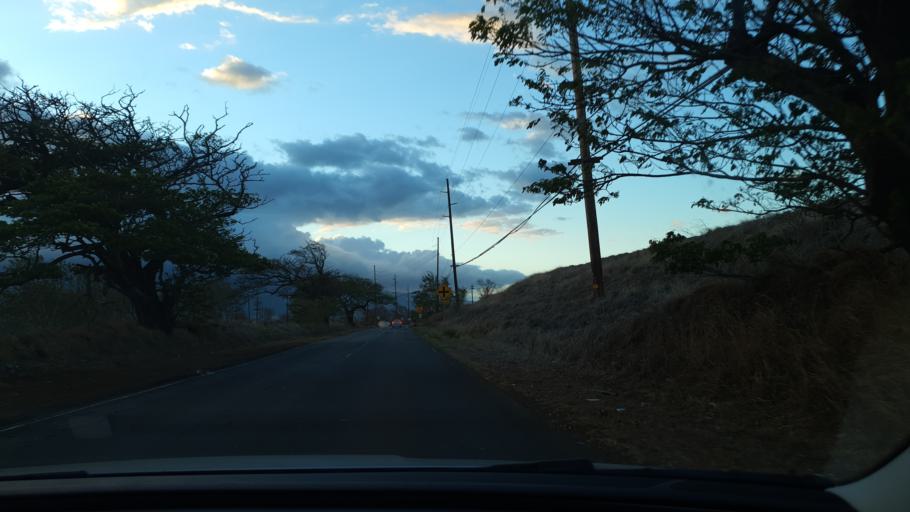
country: US
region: Hawaii
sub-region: Maui County
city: Kahului
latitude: 20.8714
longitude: -156.4383
